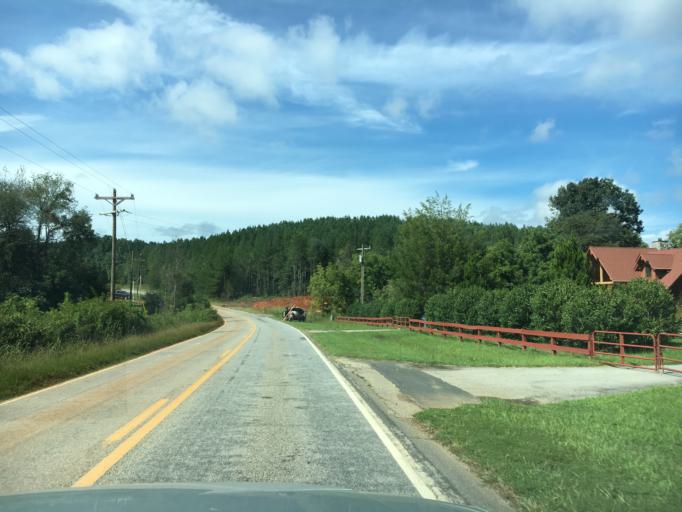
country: US
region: North Carolina
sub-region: Polk County
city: Columbus
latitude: 35.3058
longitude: -82.1642
